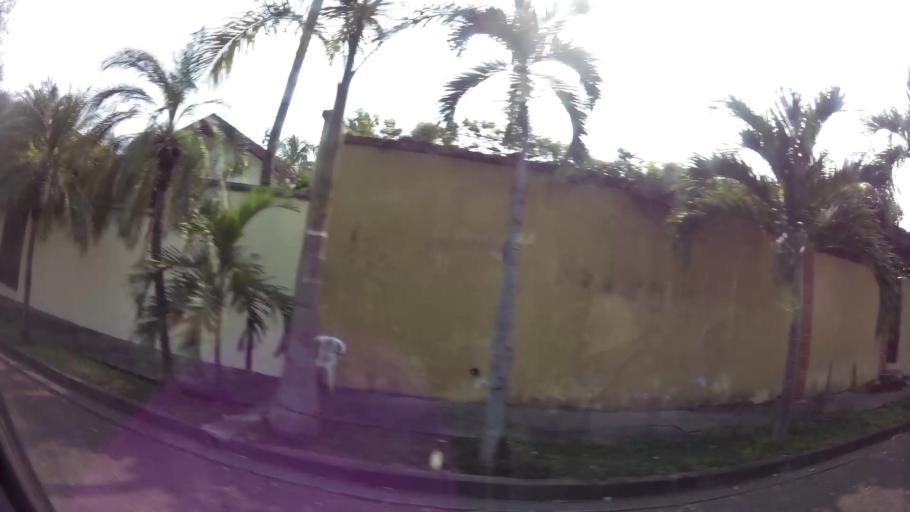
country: HN
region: Cortes
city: Armenta
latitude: 15.4944
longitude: -88.0473
